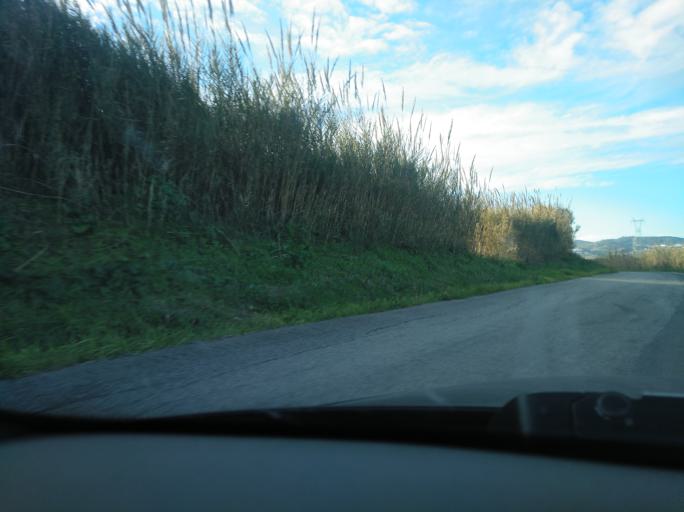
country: PT
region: Lisbon
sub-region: Loures
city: Unhos
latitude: 38.8333
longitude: -9.1212
